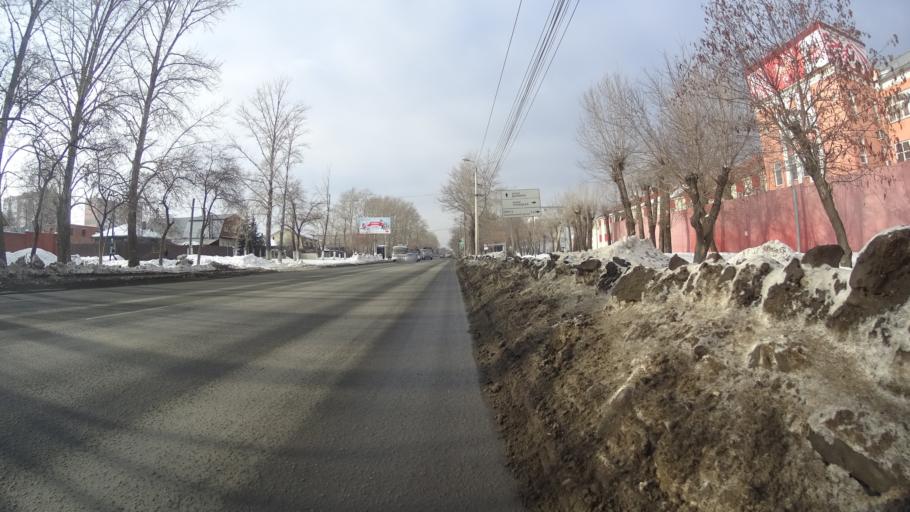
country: RU
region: Chelyabinsk
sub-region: Gorod Chelyabinsk
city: Chelyabinsk
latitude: 55.1234
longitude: 61.3743
